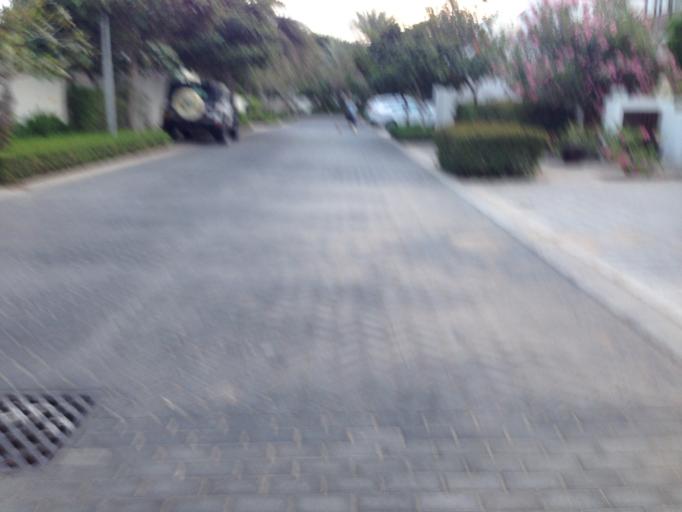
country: OM
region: Muhafazat Masqat
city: As Sib al Jadidah
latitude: 23.6272
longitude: 58.2692
